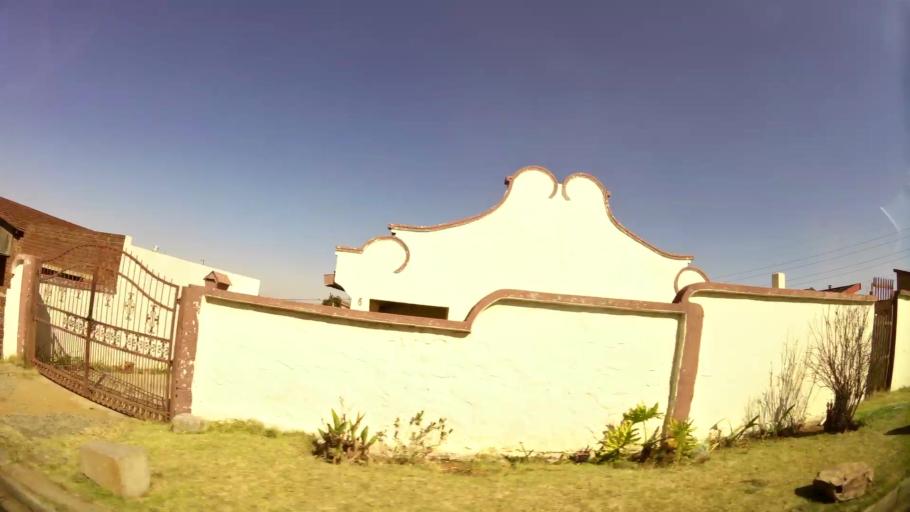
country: ZA
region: Gauteng
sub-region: City of Johannesburg Metropolitan Municipality
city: Johannesburg
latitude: -26.1875
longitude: 27.9596
